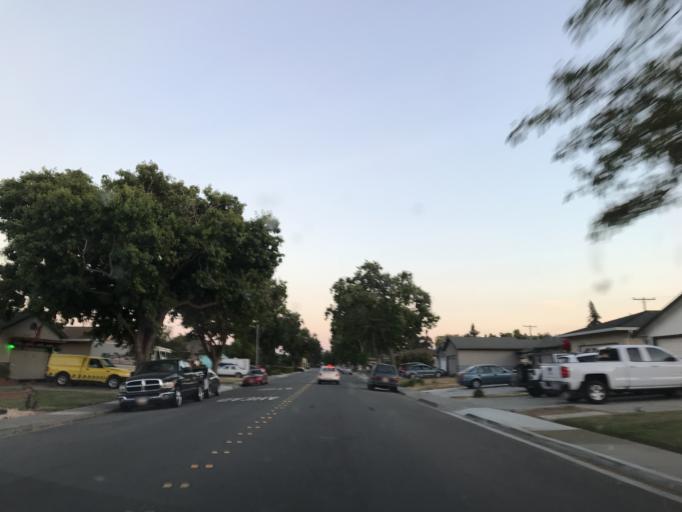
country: US
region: California
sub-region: Santa Clara County
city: Milpitas
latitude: 37.4340
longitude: -121.9154
